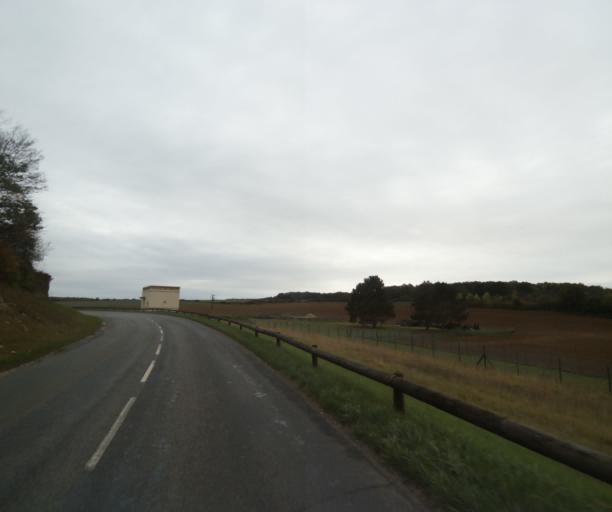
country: FR
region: Centre
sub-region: Departement d'Eure-et-Loir
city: Vert-en-Drouais
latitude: 48.7511
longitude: 1.3118
